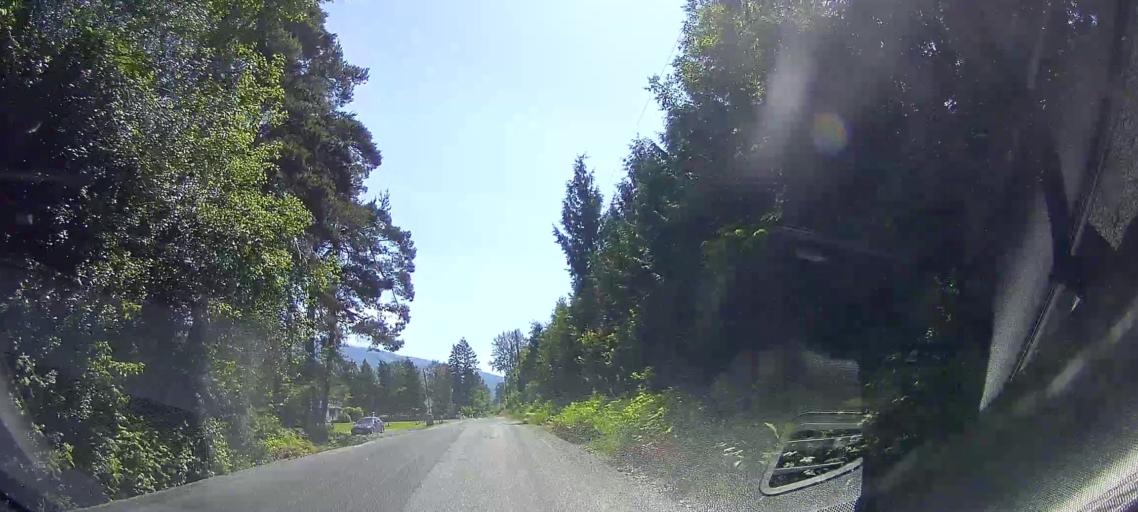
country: US
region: Washington
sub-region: Skagit County
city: Sedro-Woolley
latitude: 48.5585
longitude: -122.2667
